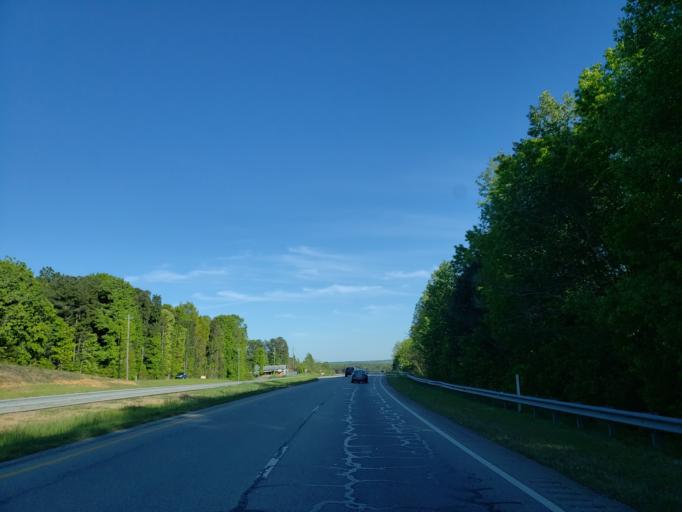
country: US
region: Georgia
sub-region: Paulding County
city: Dallas
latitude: 33.9232
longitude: -84.9359
